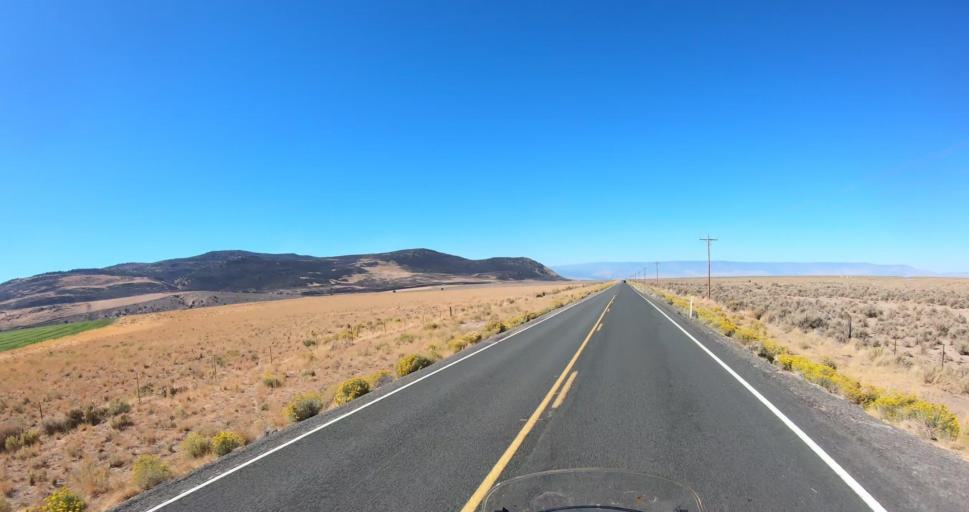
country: US
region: Oregon
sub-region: Lake County
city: Lakeview
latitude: 42.7069
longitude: -120.5538
